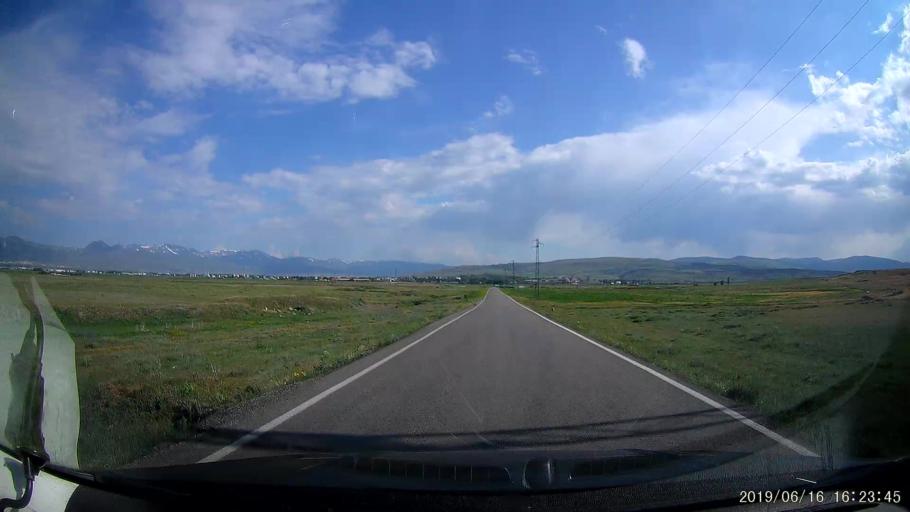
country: TR
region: Erzurum
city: Ilica
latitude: 39.9743
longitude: 41.1055
